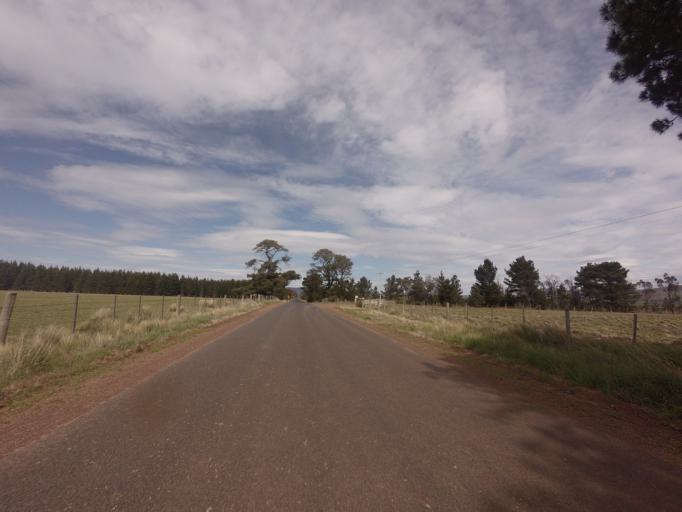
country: AU
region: Tasmania
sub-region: Northern Midlands
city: Evandale
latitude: -41.8614
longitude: 147.3464
